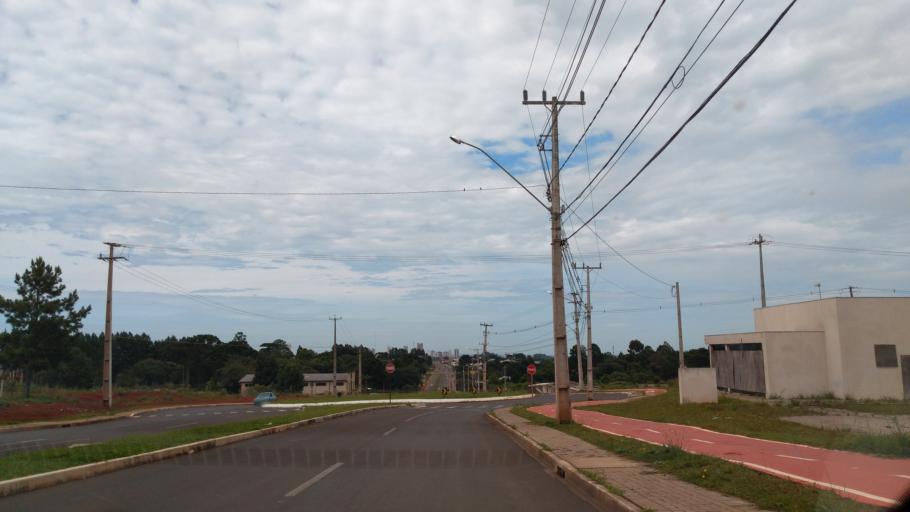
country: BR
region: Parana
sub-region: Guarapuava
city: Guarapuava
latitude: -25.3670
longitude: -51.4360
